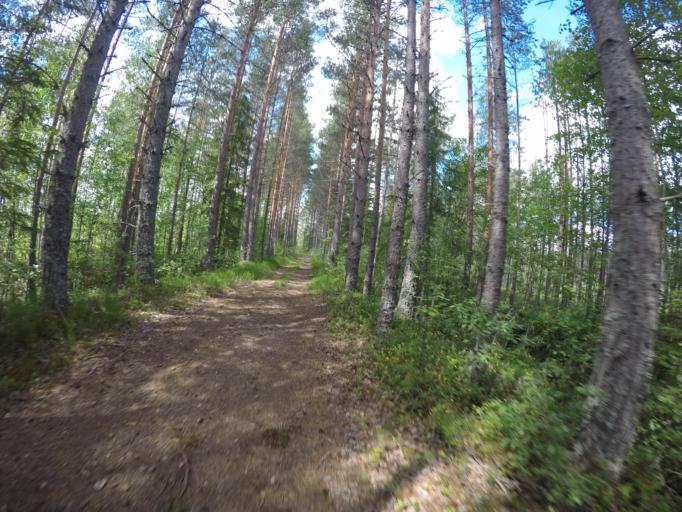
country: SE
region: Vaermland
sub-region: Filipstads Kommun
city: Lesjofors
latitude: 60.1399
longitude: 14.2885
